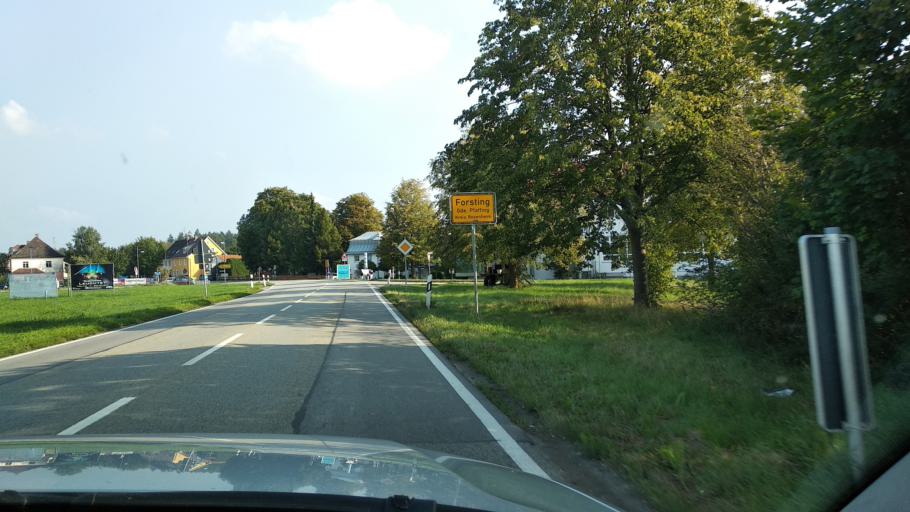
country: DE
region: Bavaria
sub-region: Upper Bavaria
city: Pfaffing
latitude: 48.0825
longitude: 12.0892
